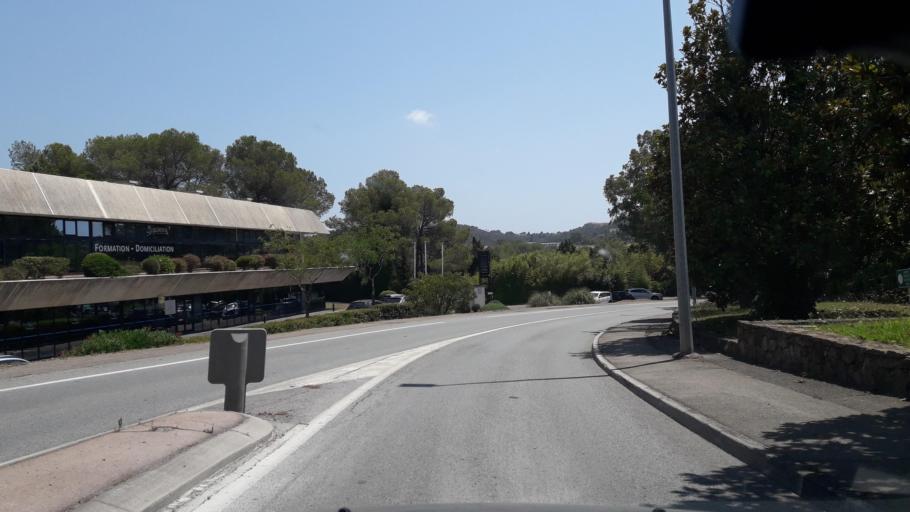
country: FR
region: Provence-Alpes-Cote d'Azur
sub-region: Departement du Var
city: Saint-Raphael
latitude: 43.4404
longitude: 6.7825
